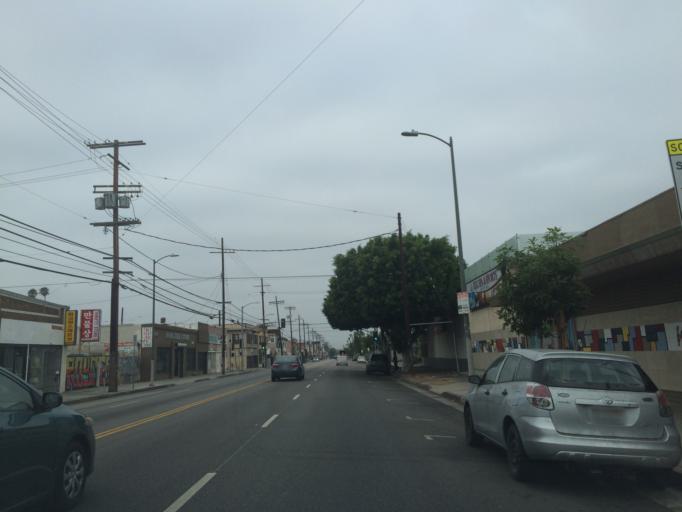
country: US
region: California
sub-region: Los Angeles County
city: Silver Lake
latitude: 34.0472
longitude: -118.3041
